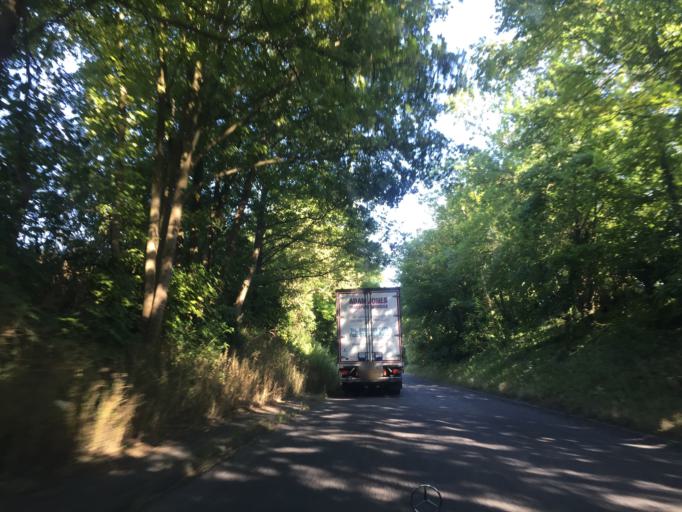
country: GB
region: England
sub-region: Oxfordshire
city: Thame
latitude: 51.7006
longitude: -0.9918
